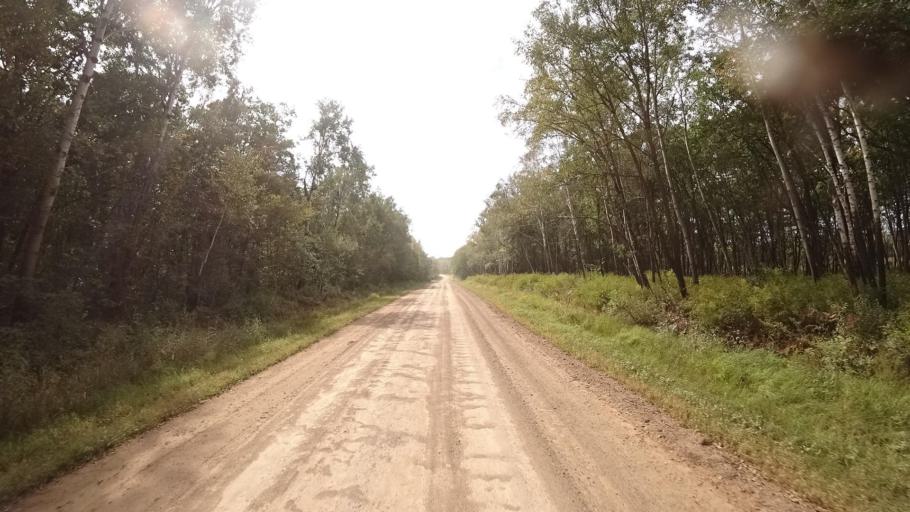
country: RU
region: Primorskiy
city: Yakovlevka
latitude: 44.5566
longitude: 133.5872
